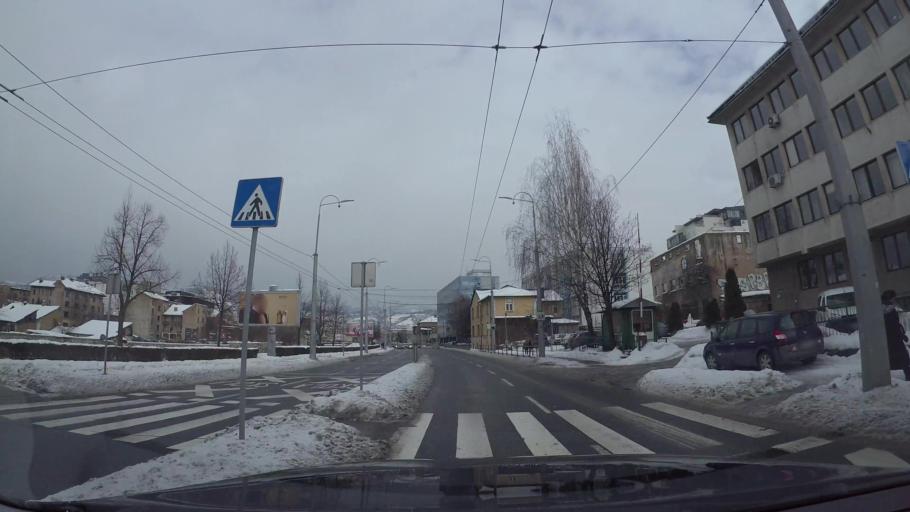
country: BA
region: Federation of Bosnia and Herzegovina
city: Kobilja Glava
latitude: 43.8534
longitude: 18.4092
